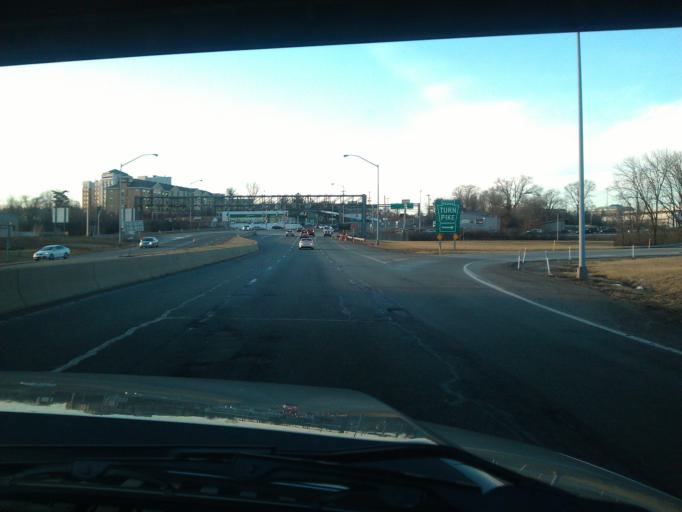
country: US
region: Pennsylvania
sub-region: Montgomery County
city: Plymouth Meeting
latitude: 40.1096
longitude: -75.2839
